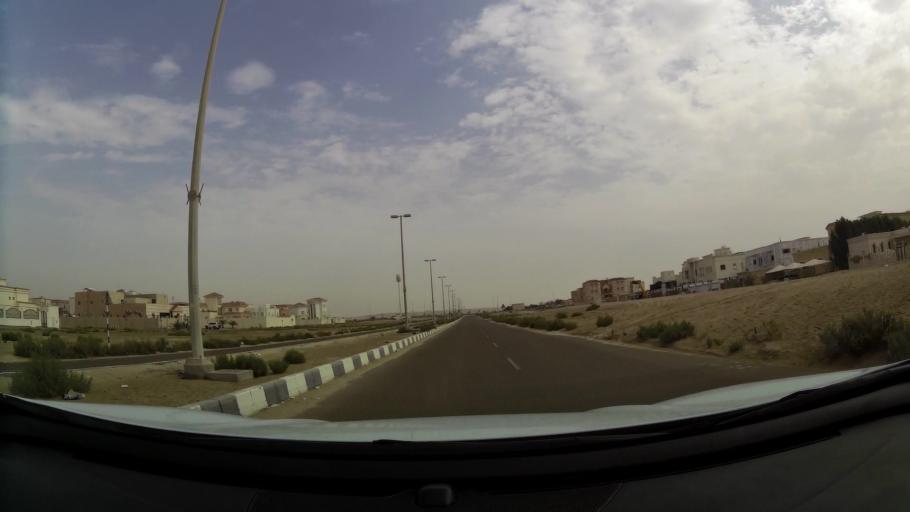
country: AE
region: Abu Dhabi
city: Abu Dhabi
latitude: 24.3079
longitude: 54.6557
